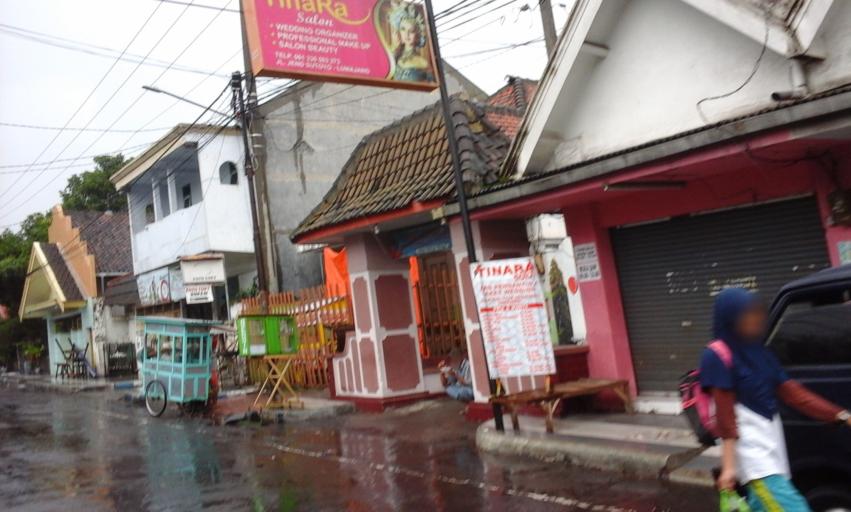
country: ID
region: East Java
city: Lumajang
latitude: -8.1334
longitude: 113.2261
